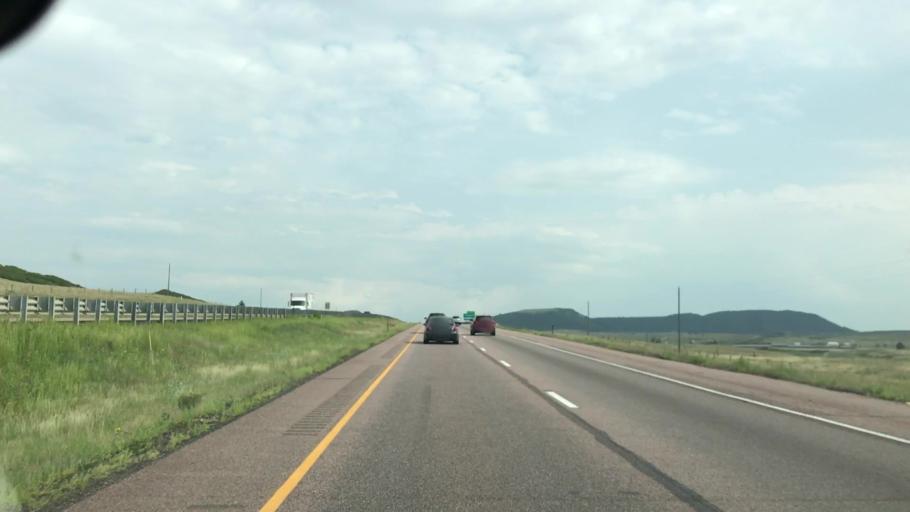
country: US
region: Colorado
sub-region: El Paso County
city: Woodmoor
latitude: 39.1986
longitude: -104.8551
